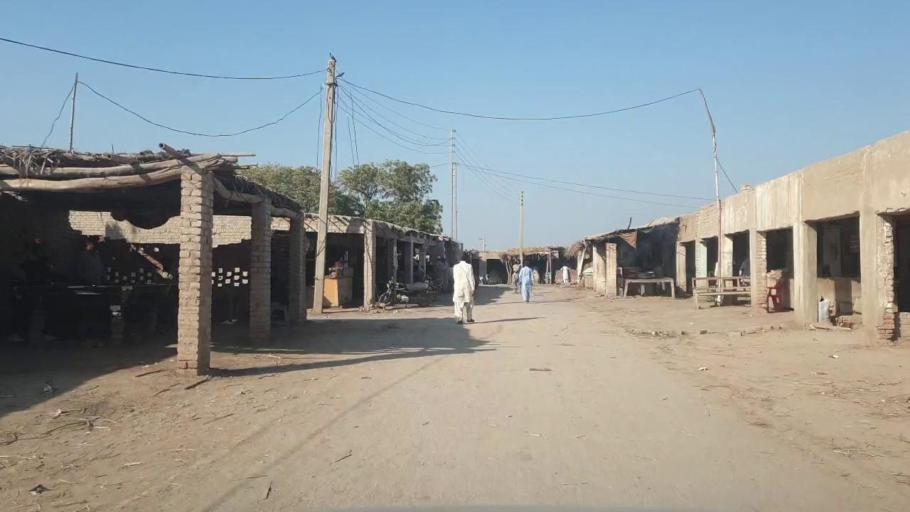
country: PK
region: Sindh
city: Chambar
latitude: 25.2936
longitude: 68.8637
